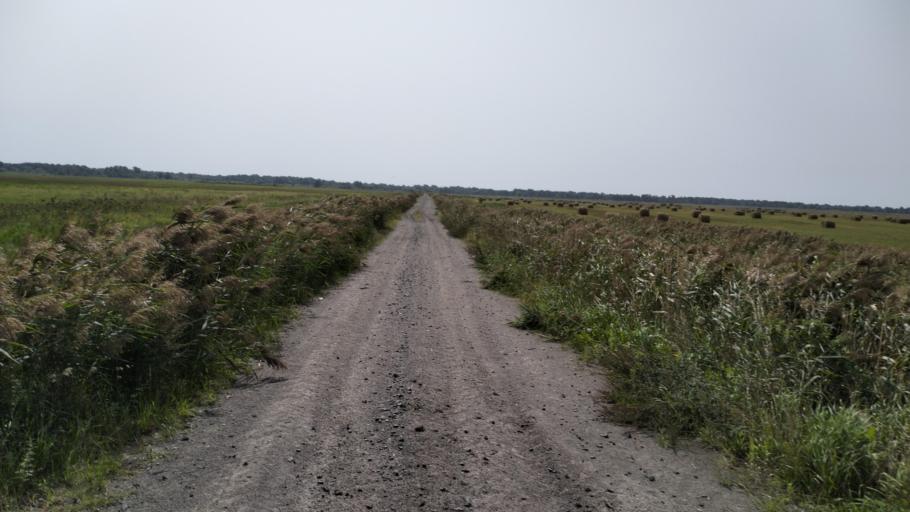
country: BY
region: Brest
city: Davyd-Haradok
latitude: 51.9815
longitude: 27.1750
